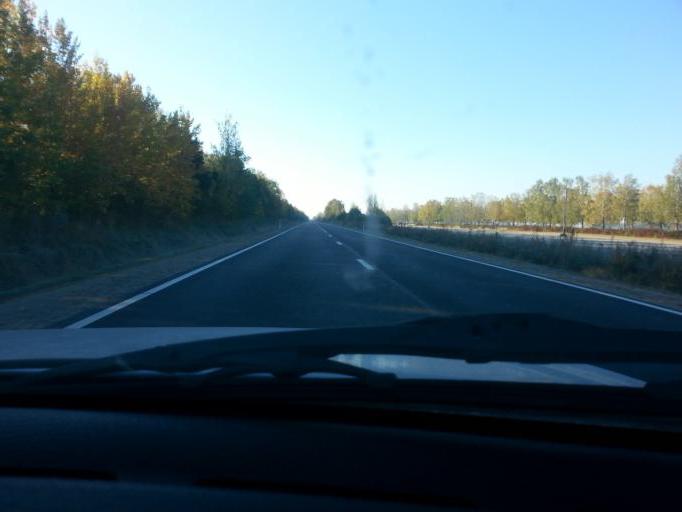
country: LV
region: Jelgava
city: Jelgava
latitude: 56.5020
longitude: 23.7002
